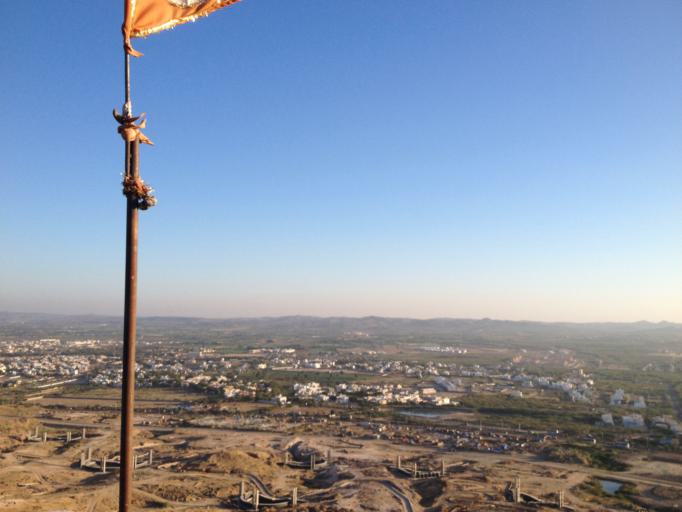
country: IN
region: Gujarat
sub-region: Kachchh
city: Bhuj
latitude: 23.2448
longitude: 69.6867
